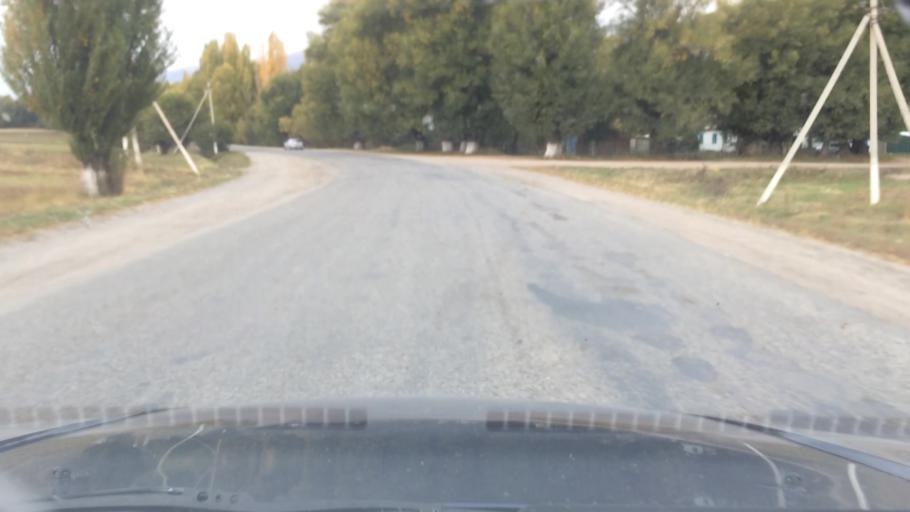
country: KG
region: Ysyk-Koel
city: Tyup
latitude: 42.7870
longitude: 78.2629
